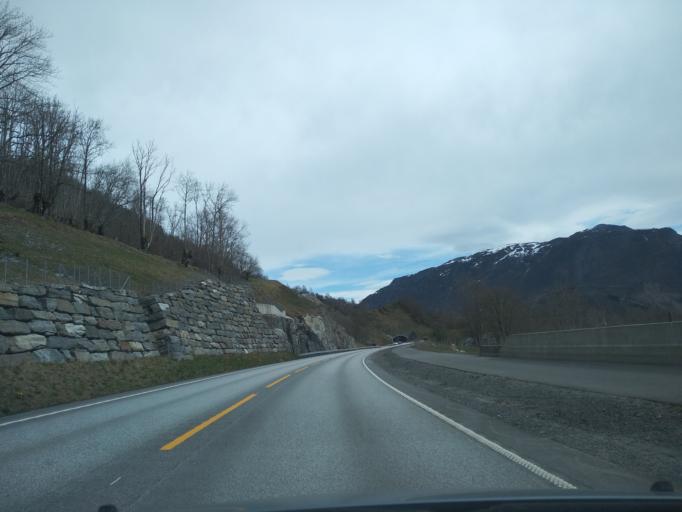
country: NO
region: Hordaland
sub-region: Etne
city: Etne
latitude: 59.7087
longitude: 6.0684
